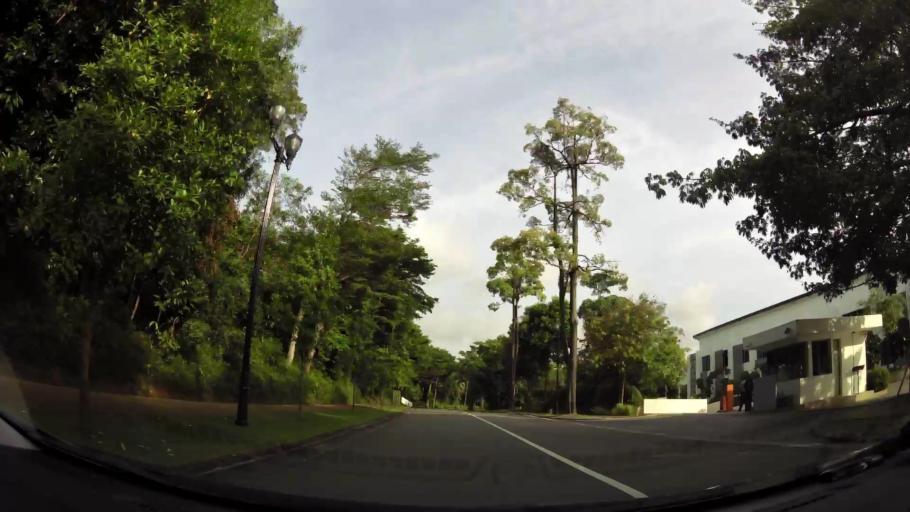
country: SG
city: Singapore
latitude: 1.2457
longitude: 103.8394
